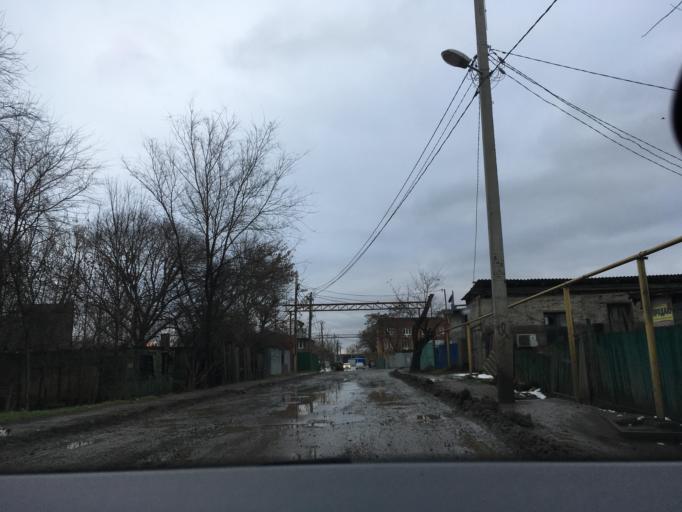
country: RU
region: Rostov
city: Rostov-na-Donu
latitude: 47.2107
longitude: 39.7178
